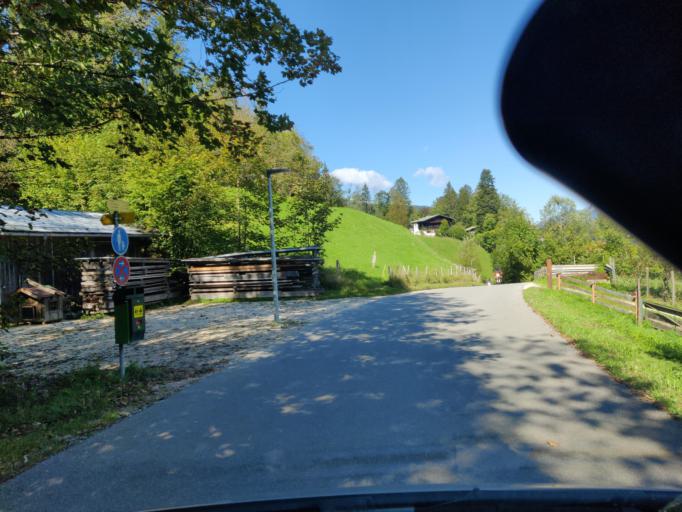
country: DE
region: Bavaria
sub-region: Upper Bavaria
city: Schoenau am Koenigssee
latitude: 47.5917
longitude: 12.9845
